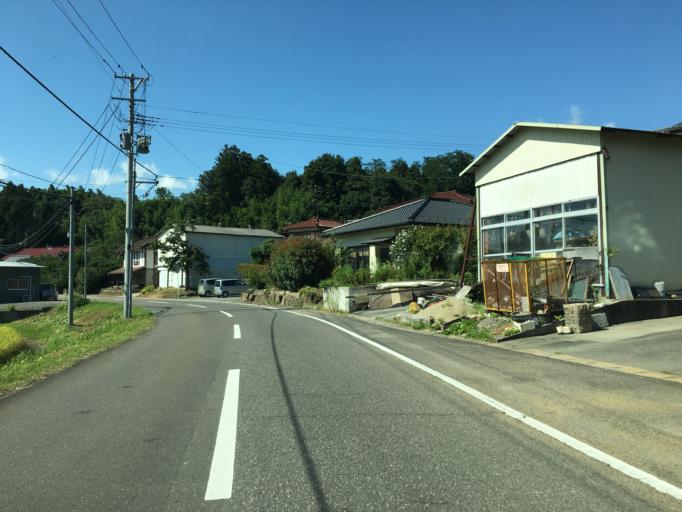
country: JP
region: Fukushima
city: Sukagawa
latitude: 37.2829
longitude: 140.4284
